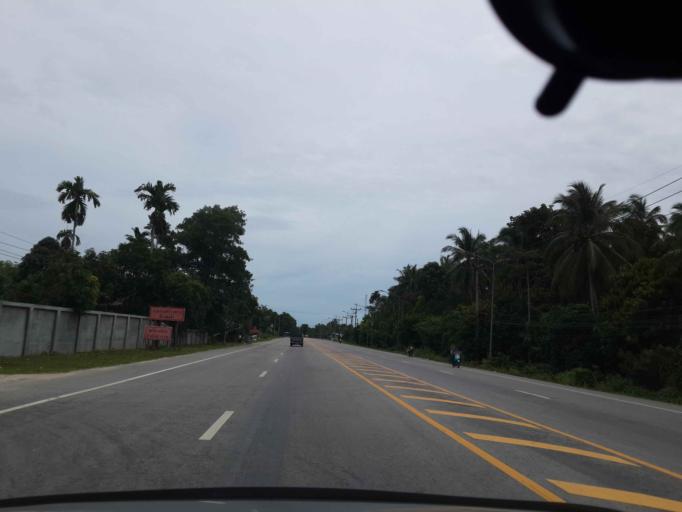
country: TH
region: Narathiwat
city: Yi-ngo
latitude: 6.3956
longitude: 101.6942
